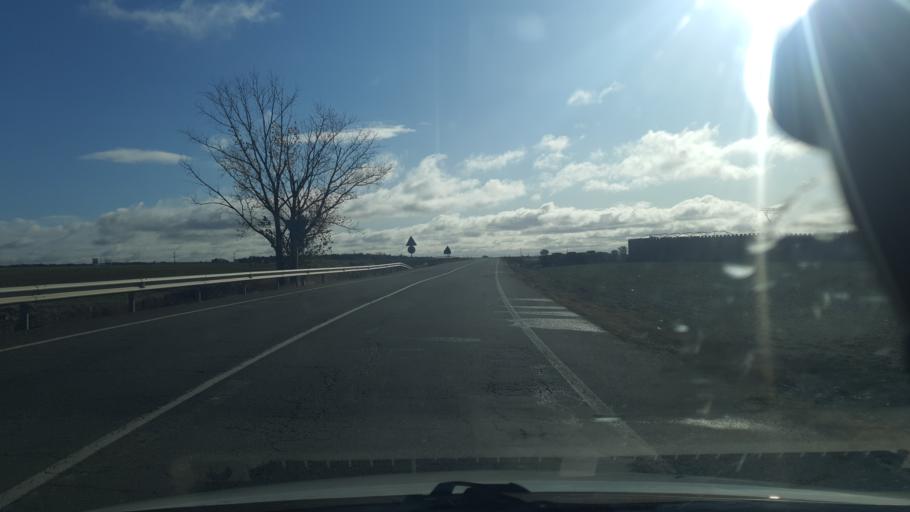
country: ES
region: Castille and Leon
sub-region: Provincia de Segovia
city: Martin Munoz de la Dehesa
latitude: 41.0502
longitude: -4.6970
